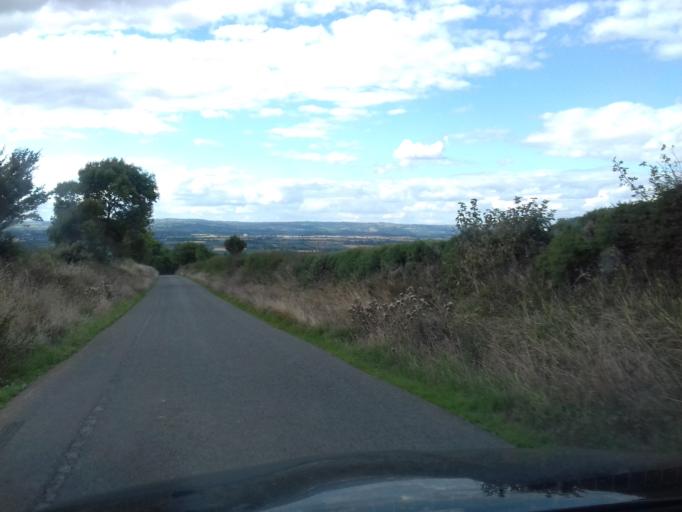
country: IE
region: Leinster
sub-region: Kilkenny
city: Graiguenamanagh
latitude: 52.5742
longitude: -7.0070
